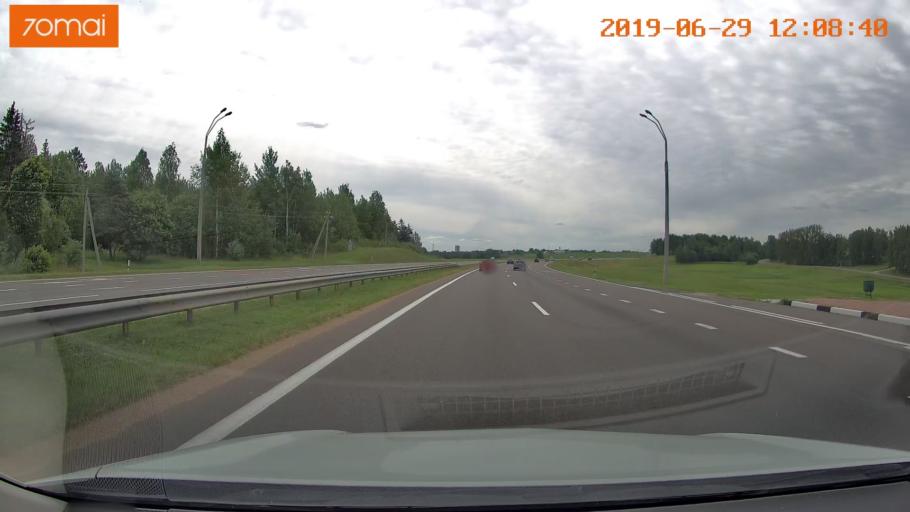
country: BY
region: Minsk
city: Samakhvalavichy
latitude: 53.7039
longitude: 27.5250
